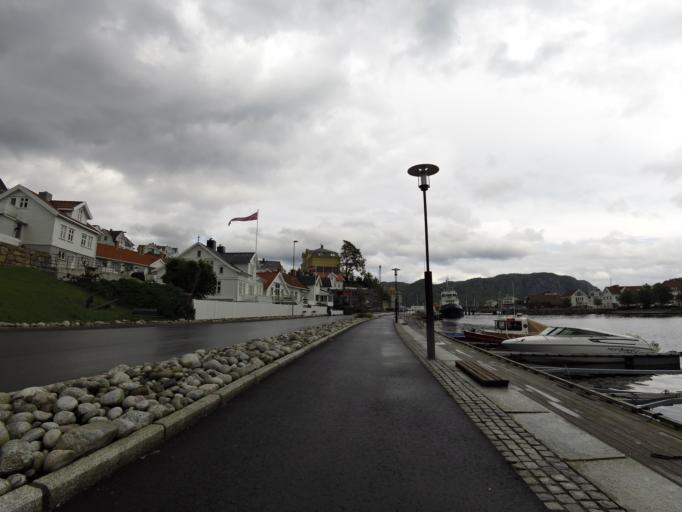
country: NO
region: Vest-Agder
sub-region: Farsund
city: Farsund
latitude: 58.0916
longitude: 6.8053
